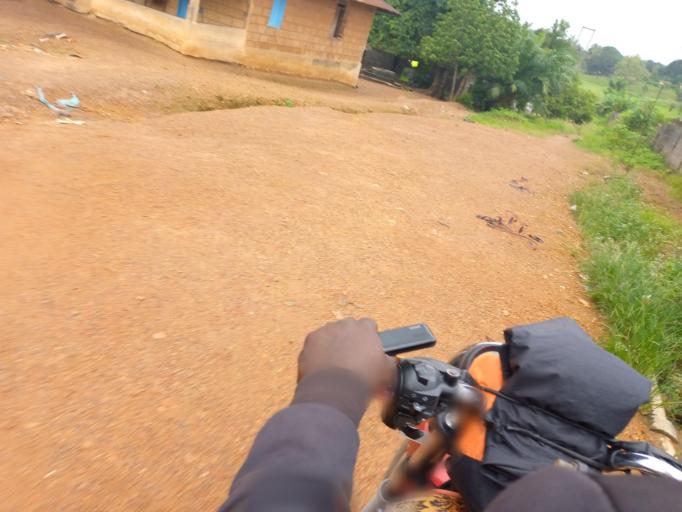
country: SL
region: Eastern Province
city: Kenema
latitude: 7.8677
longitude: -11.1867
